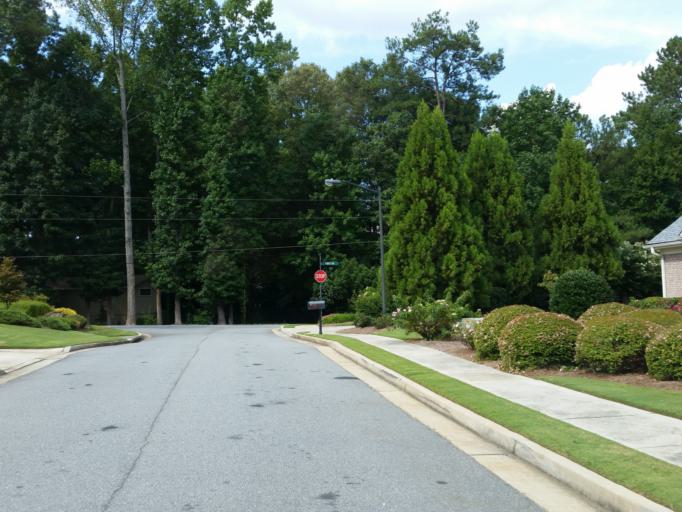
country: US
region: Georgia
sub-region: Cobb County
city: Marietta
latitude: 34.0098
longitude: -84.4925
